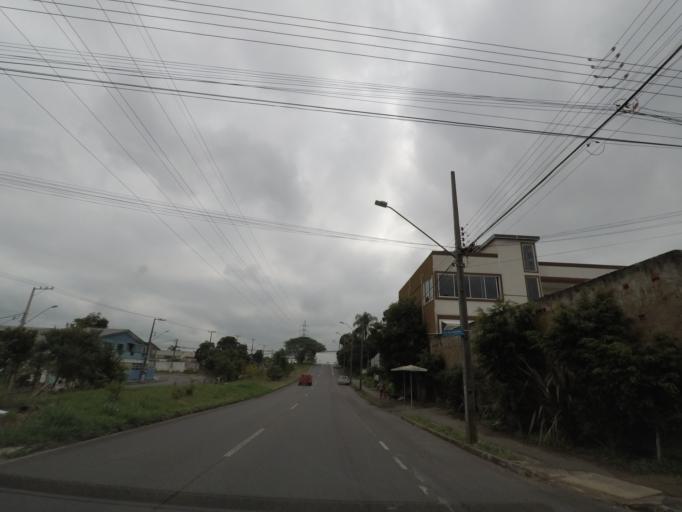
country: BR
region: Parana
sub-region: Curitiba
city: Curitiba
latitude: -25.5011
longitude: -49.3161
